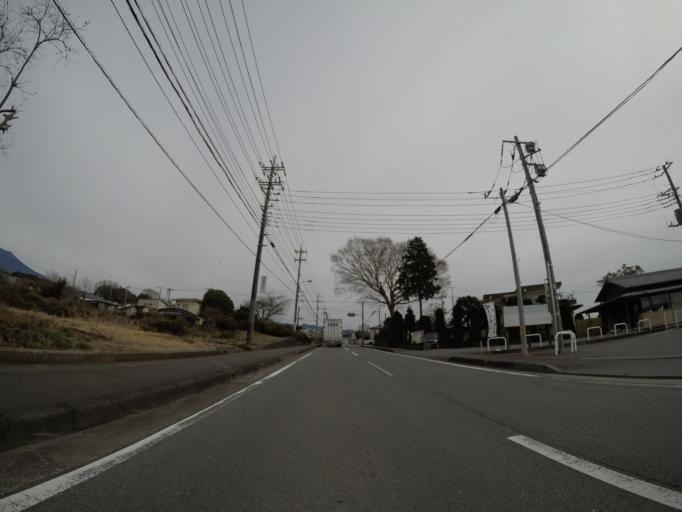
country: JP
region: Shizuoka
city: Fujinomiya
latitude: 35.2192
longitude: 138.6509
